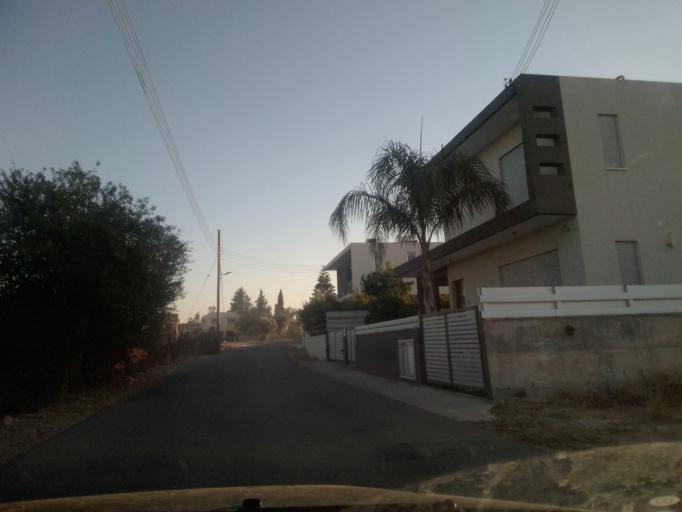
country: CY
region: Limassol
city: Ypsonas
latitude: 34.6820
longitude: 32.9601
